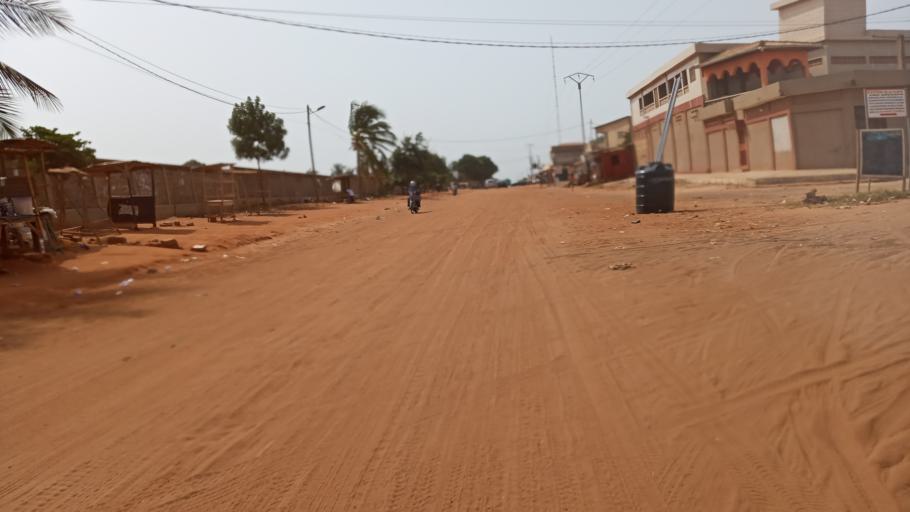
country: TG
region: Maritime
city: Lome
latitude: 6.2090
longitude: 1.1596
